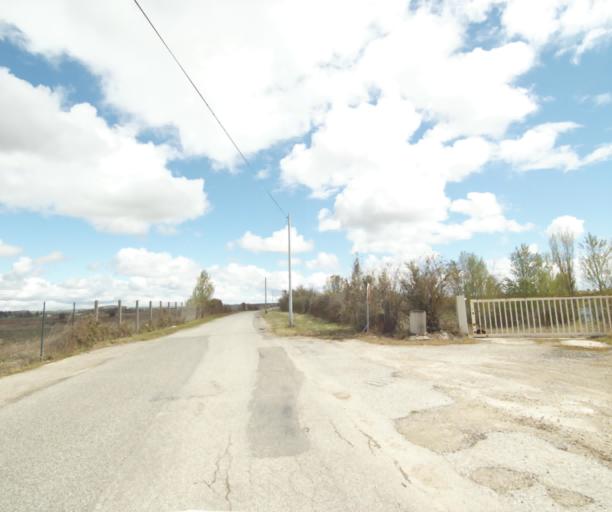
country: FR
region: Midi-Pyrenees
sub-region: Departement de l'Ariege
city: Saverdun
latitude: 43.2374
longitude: 1.5986
